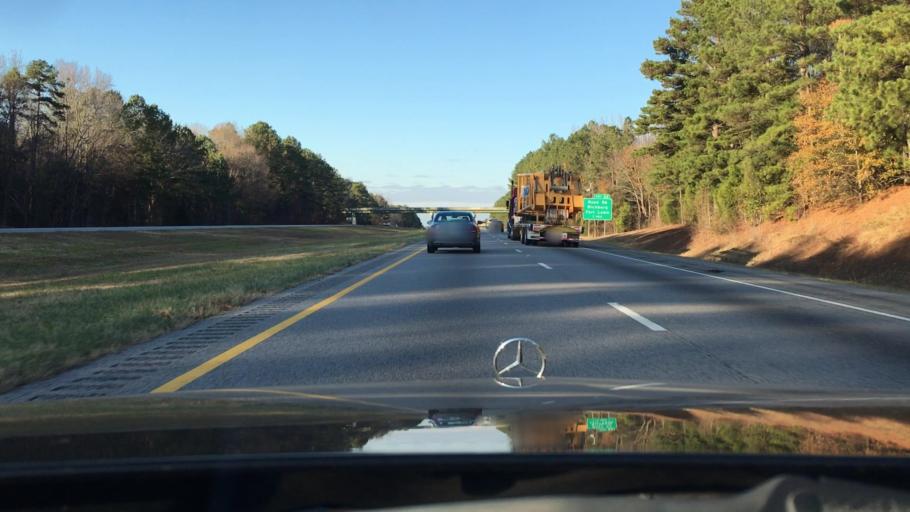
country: US
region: South Carolina
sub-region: Chester County
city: Eureka Mill
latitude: 34.6936
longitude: -81.0295
